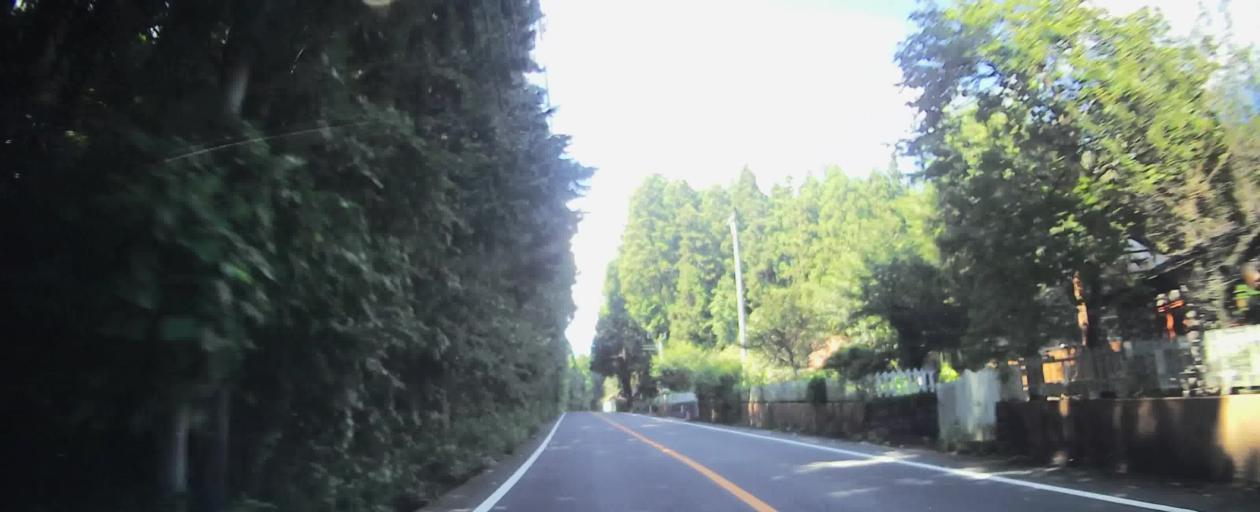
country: JP
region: Gunma
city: Kanekomachi
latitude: 36.4300
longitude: 138.9261
